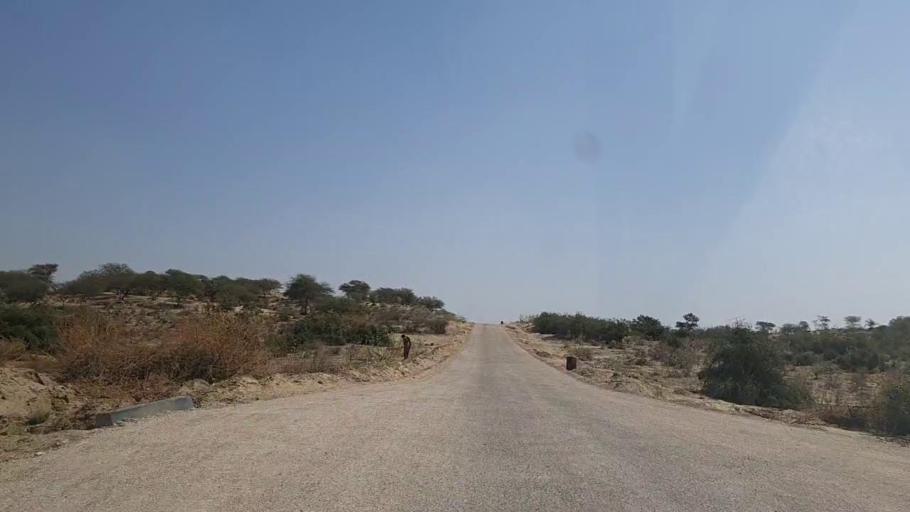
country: PK
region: Sindh
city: Diplo
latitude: 24.4804
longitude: 69.4970
